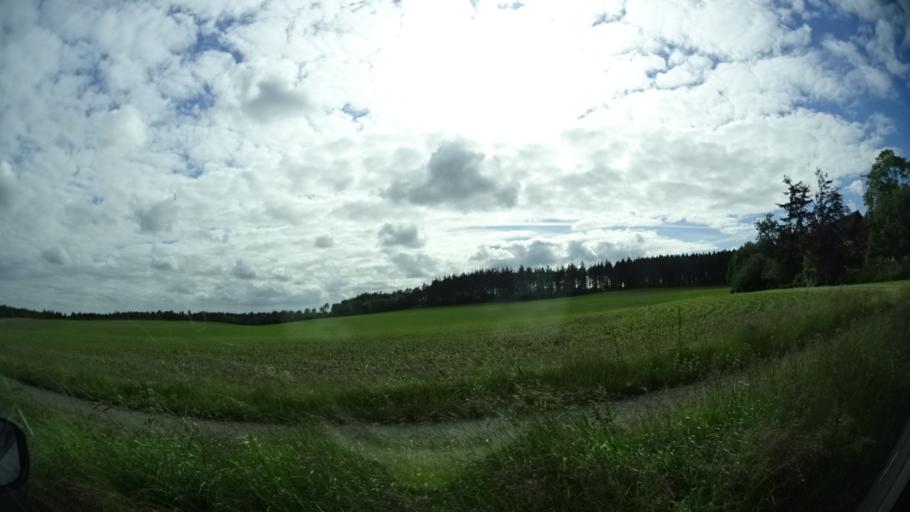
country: DK
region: Central Jutland
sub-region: Norddjurs Kommune
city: Grenaa
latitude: 56.5095
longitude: 10.7309
